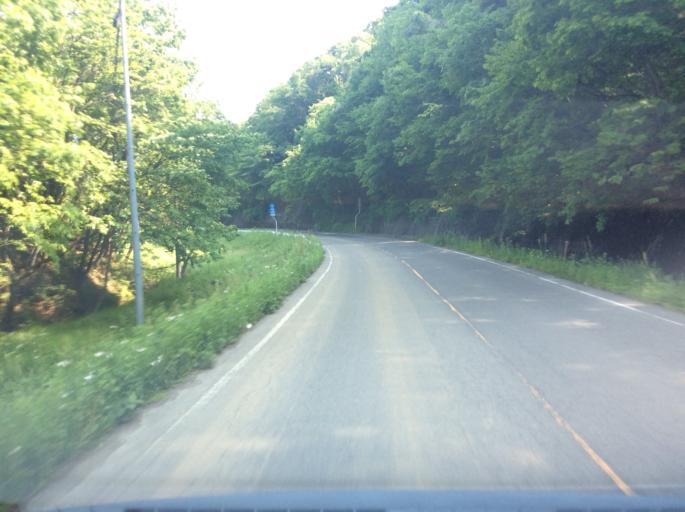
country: JP
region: Tochigi
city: Kuroiso
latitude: 37.0721
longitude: 140.2265
